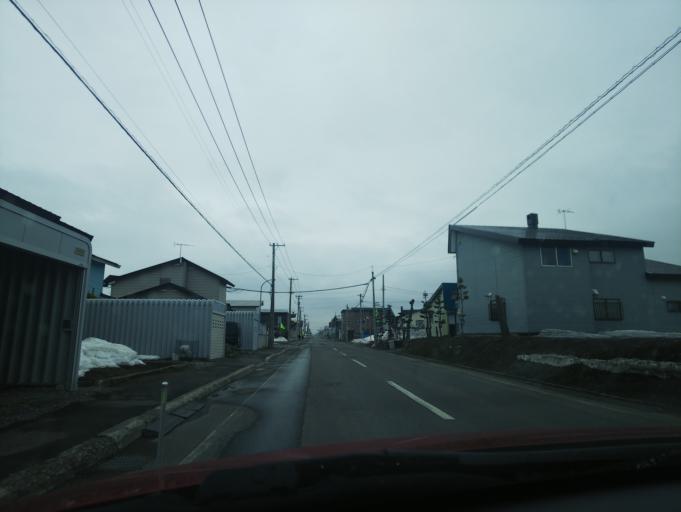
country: JP
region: Hokkaido
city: Nayoro
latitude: 44.3644
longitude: 142.4502
